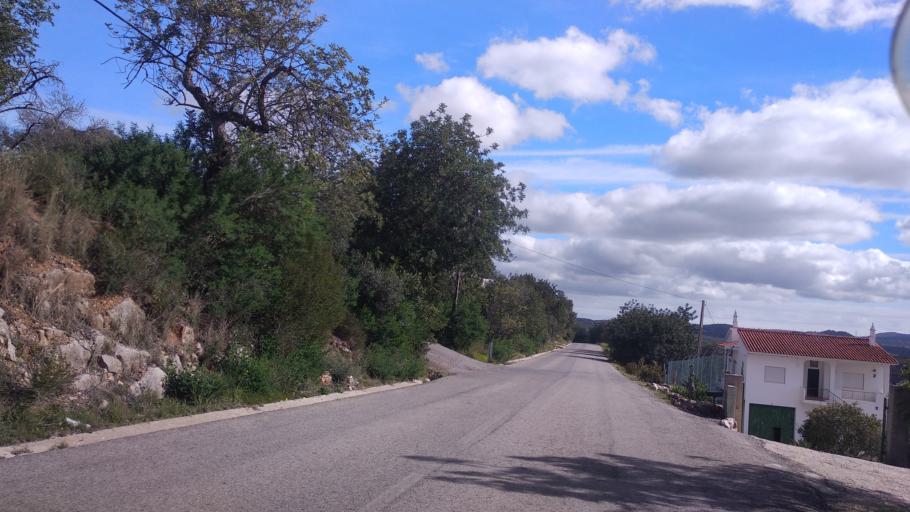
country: PT
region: Faro
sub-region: Sao Bras de Alportel
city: Sao Bras de Alportel
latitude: 37.1493
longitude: -7.9119
